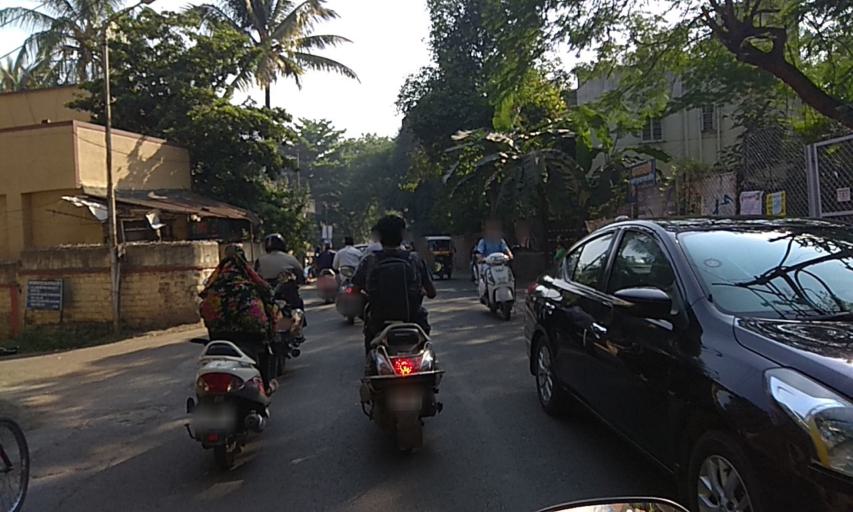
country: IN
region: Maharashtra
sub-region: Pune Division
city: Pune
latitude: 18.4785
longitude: 73.8226
